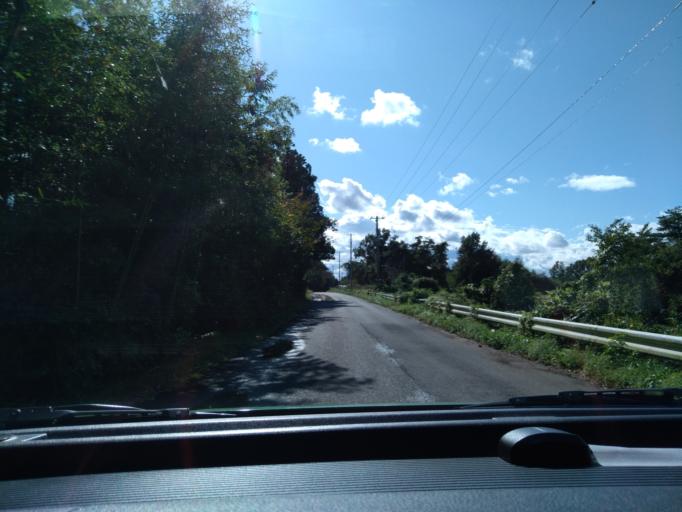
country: JP
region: Iwate
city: Ichinoseki
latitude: 38.7853
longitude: 141.2093
